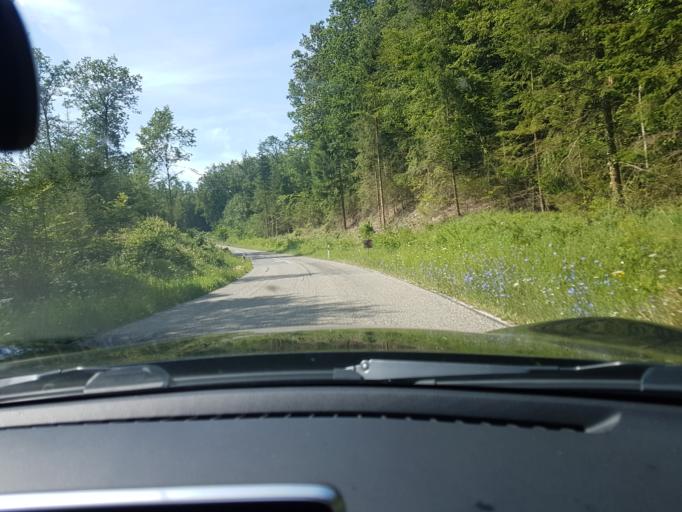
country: DE
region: Baden-Wuerttemberg
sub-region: Karlsruhe Region
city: Seckach
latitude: 49.4461
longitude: 9.3543
